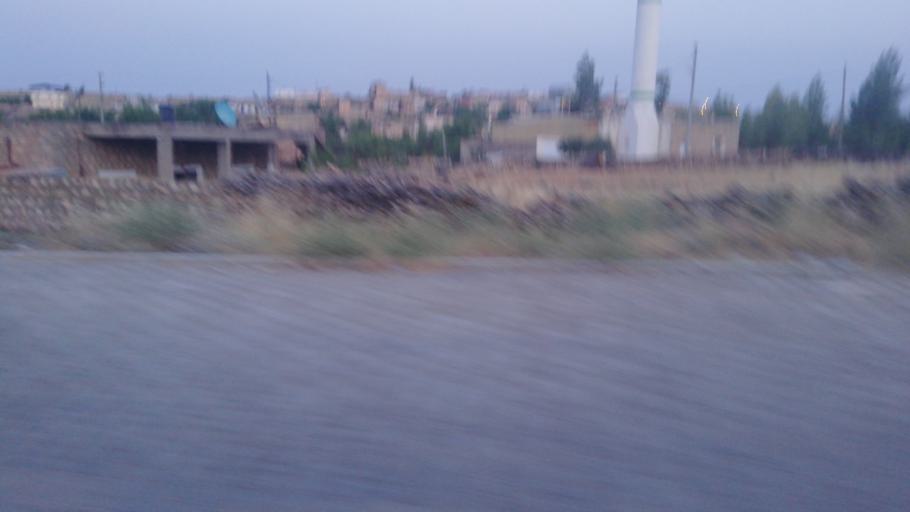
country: TR
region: Mardin
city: Kindirip
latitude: 37.4499
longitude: 41.2175
